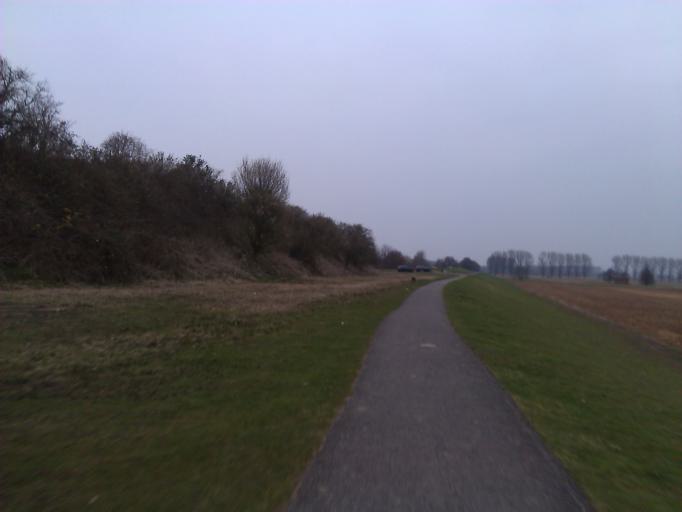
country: DE
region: North Rhine-Westphalia
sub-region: Regierungsbezirk Dusseldorf
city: Dormagen
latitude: 51.0902
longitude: 6.8524
